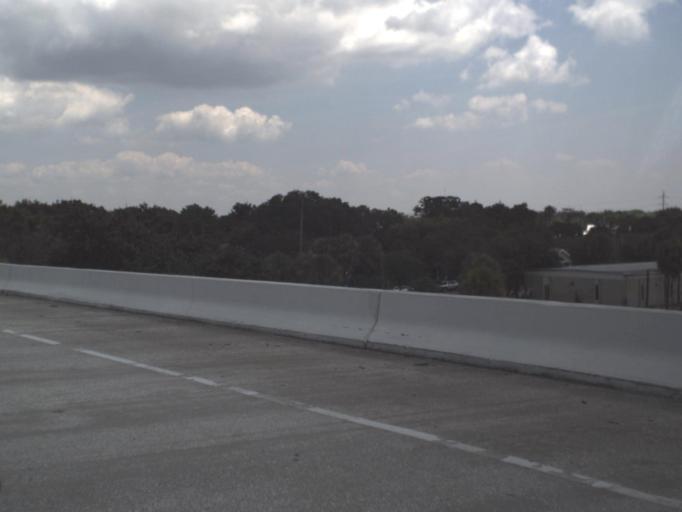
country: US
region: Florida
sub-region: Pinellas County
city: Saint Petersburg
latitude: 27.7710
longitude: -82.6580
